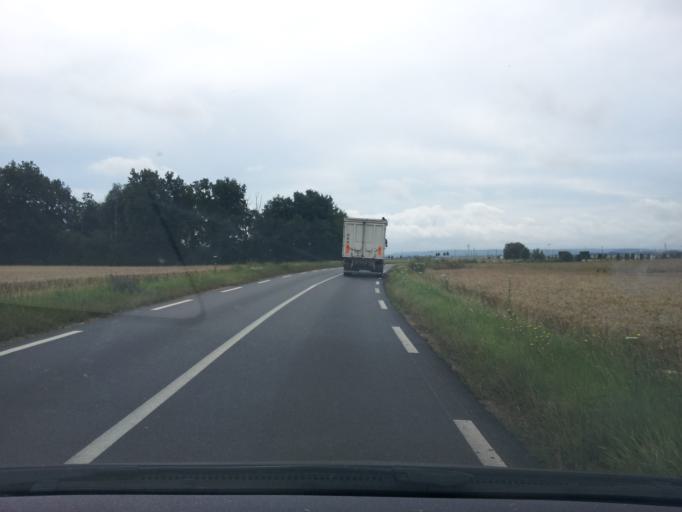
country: FR
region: Ile-de-France
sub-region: Departement de l'Essonne
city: Leudeville
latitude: 48.5694
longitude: 2.3323
